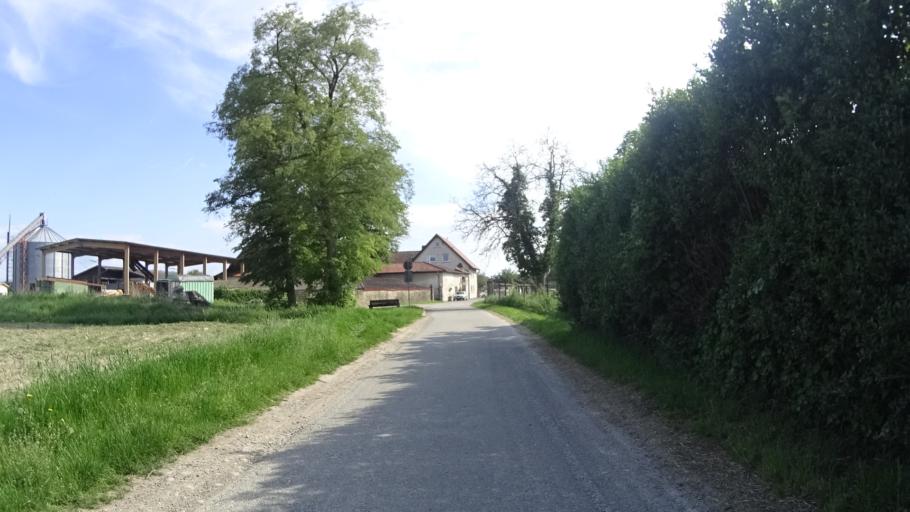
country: DE
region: Baden-Wuerttemberg
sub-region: Freiburg Region
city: Breisach am Rhein
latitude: 48.0464
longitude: 7.5835
